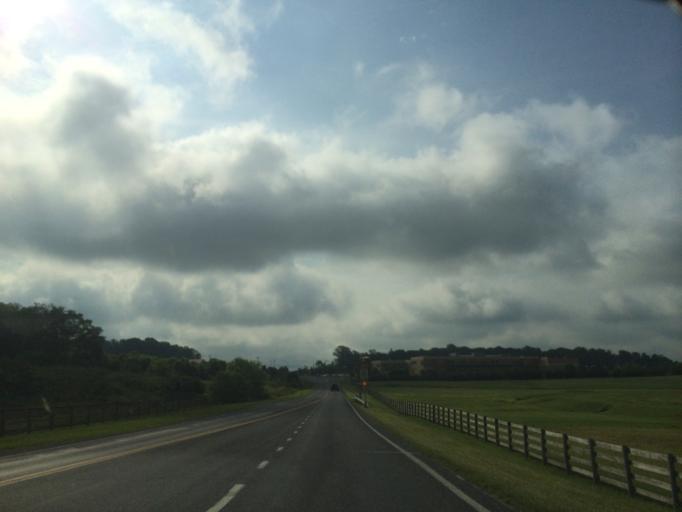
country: US
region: Maryland
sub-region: Carroll County
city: Sykesville
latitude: 39.3040
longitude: -77.0257
